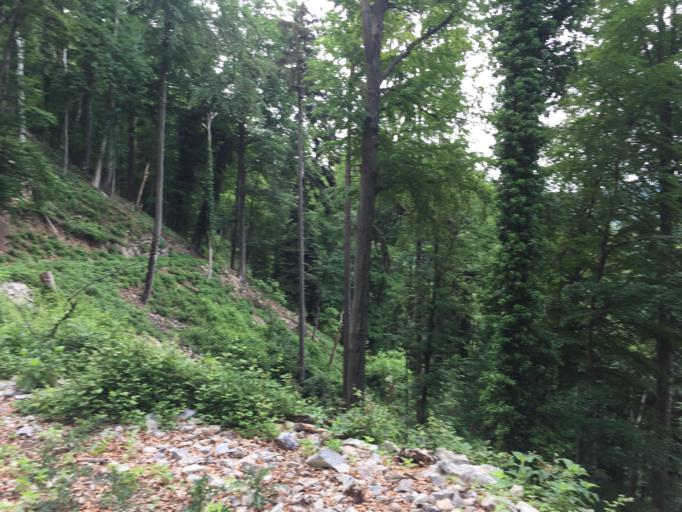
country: SI
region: Tolmin
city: Tolmin
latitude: 46.1696
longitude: 13.8418
